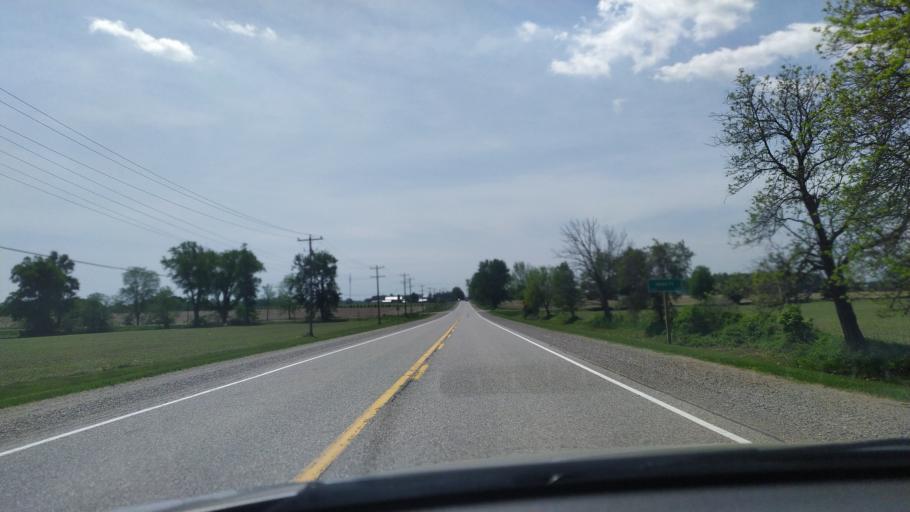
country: CA
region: Ontario
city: Dorchester
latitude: 43.0884
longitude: -81.0043
